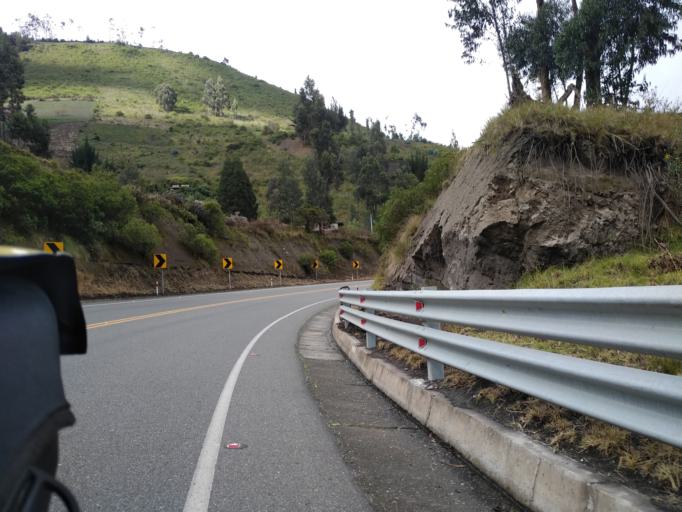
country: EC
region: Tungurahua
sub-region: Canton Quero
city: Quero
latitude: -1.4949
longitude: -78.5258
